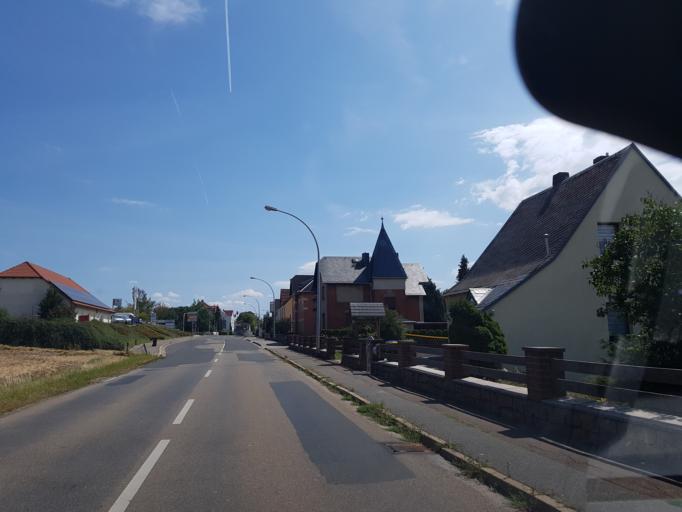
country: DE
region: Saxony
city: Hartha
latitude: 51.0818
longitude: 12.9936
